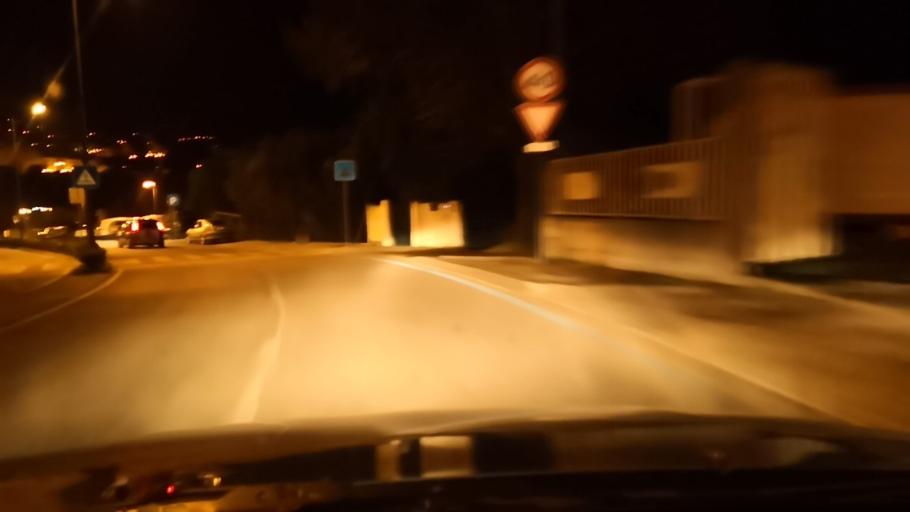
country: PT
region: Castelo Branco
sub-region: Concelho do Fundao
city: Fundao
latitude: 40.1448
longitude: -7.5012
